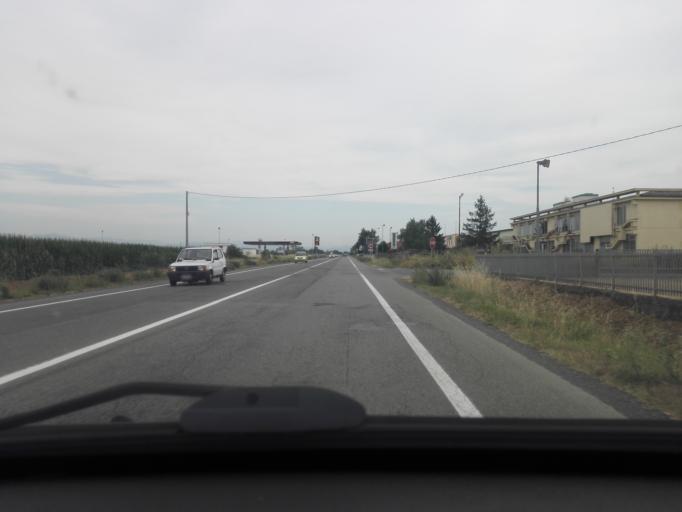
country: IT
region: Piedmont
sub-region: Provincia di Alessandria
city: Mandrogne
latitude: 44.8361
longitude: 8.7354
